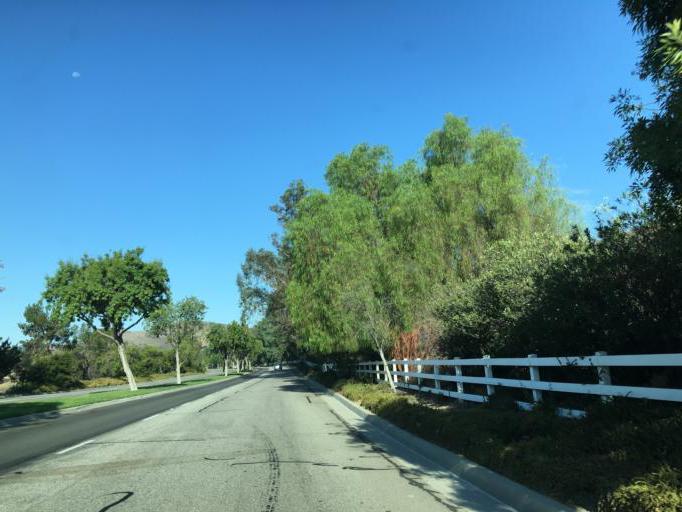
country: US
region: California
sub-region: Los Angeles County
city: Hidden Hills
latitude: 34.1521
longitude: -118.6818
